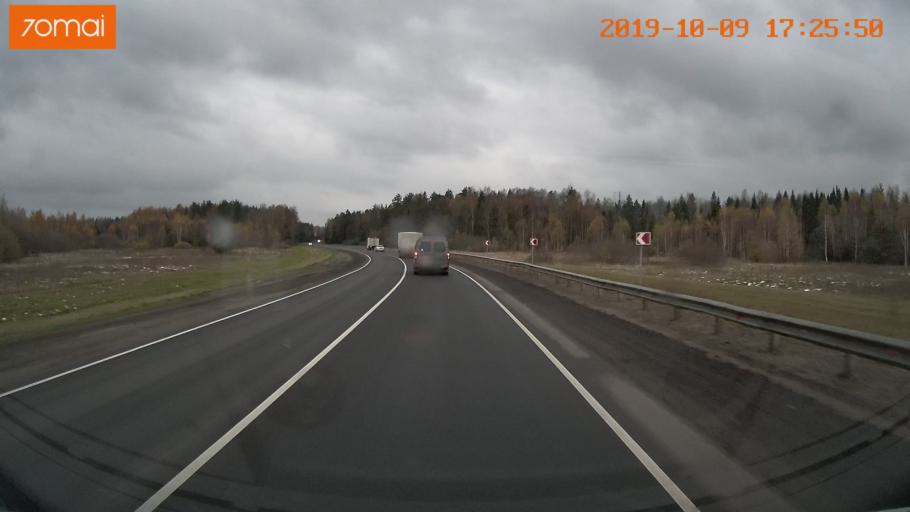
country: RU
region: Ivanovo
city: Furmanov
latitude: 57.1787
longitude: 41.0838
